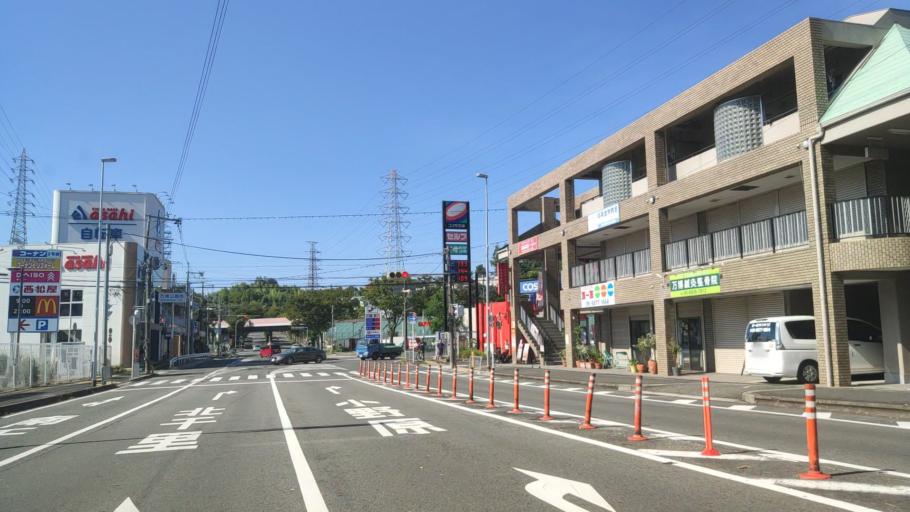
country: JP
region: Osaka
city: Suita
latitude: 34.8099
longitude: 135.5179
